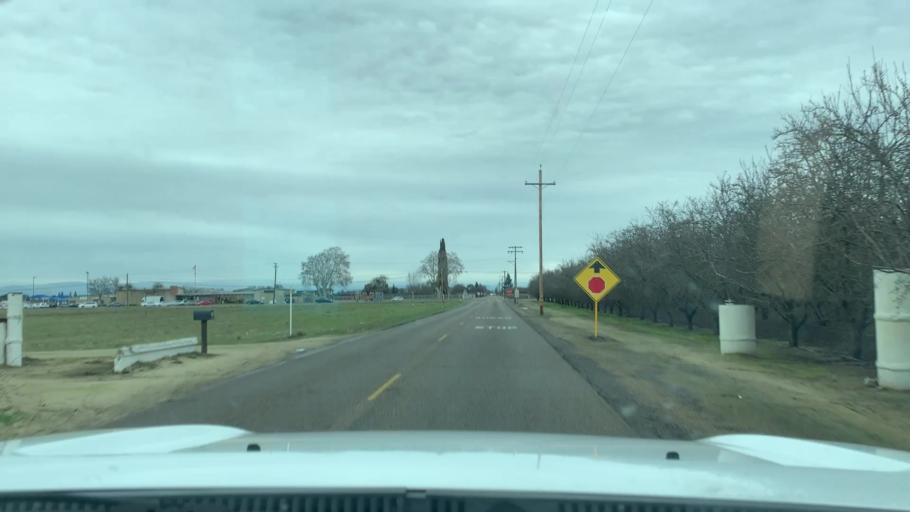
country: US
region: California
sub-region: Fresno County
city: Selma
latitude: 36.5472
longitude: -119.6851
